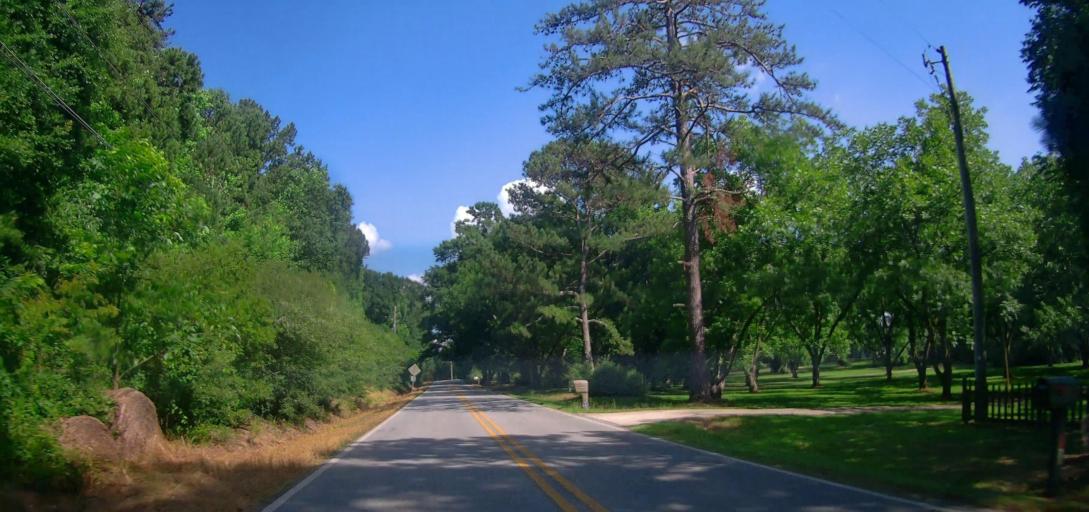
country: US
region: Georgia
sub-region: Spalding County
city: East Griffin
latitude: 33.2909
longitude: -84.2073
